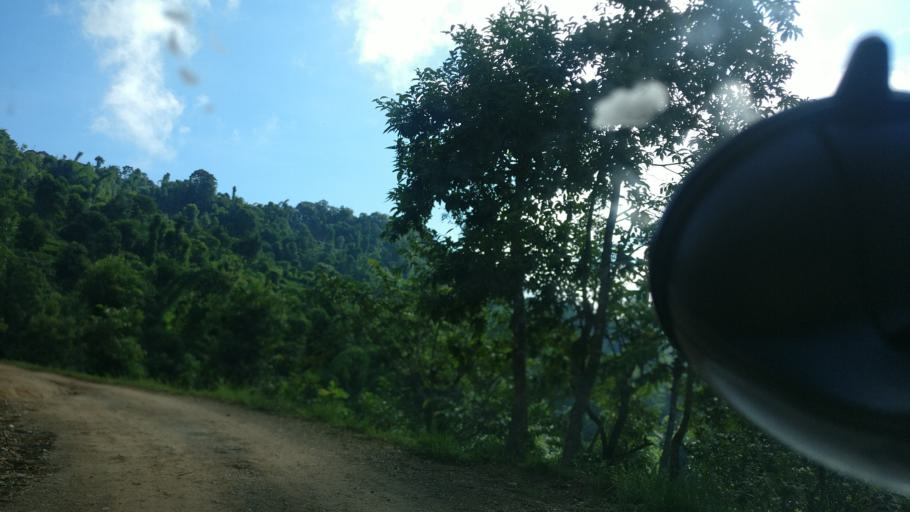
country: NP
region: Western Region
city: Baglung
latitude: 28.1366
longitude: 83.6490
